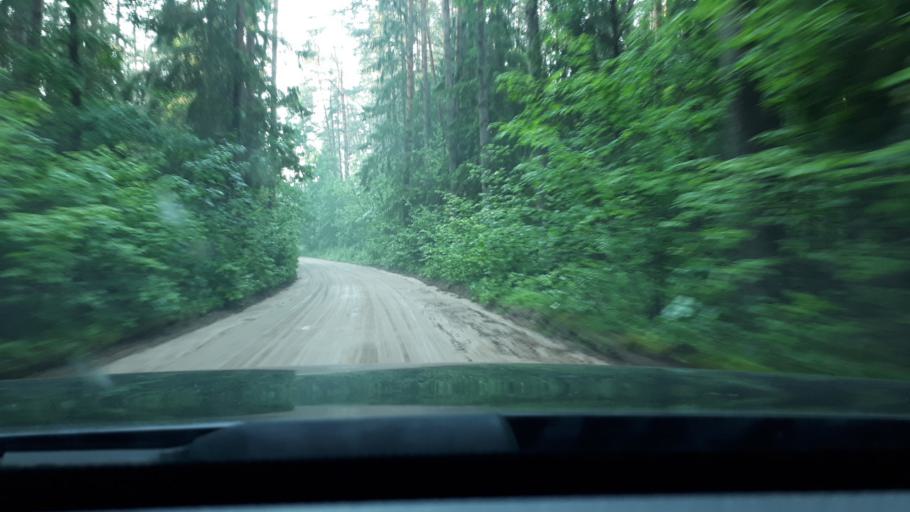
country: PL
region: Podlasie
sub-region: Powiat bialostocki
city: Suprasl
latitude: 53.2239
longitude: 23.3515
